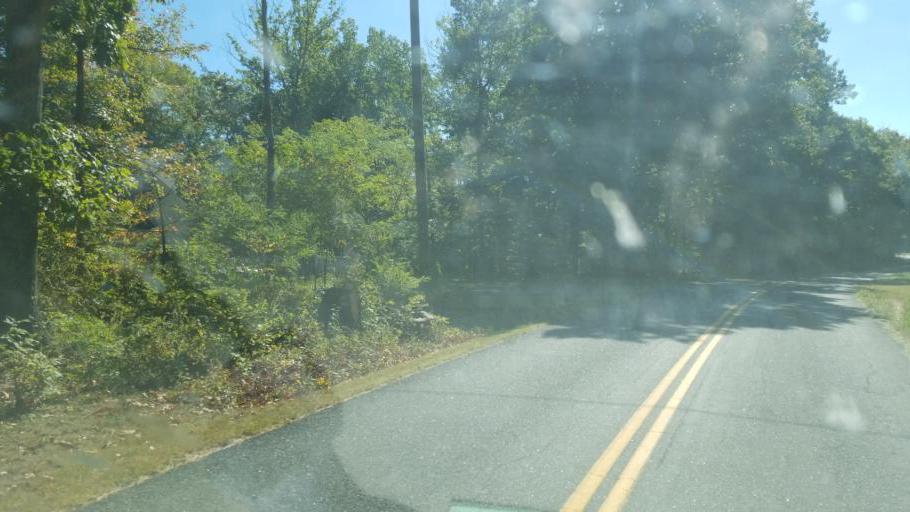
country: US
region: Virginia
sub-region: Greene County
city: Stanardsville
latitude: 38.3598
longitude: -78.4236
